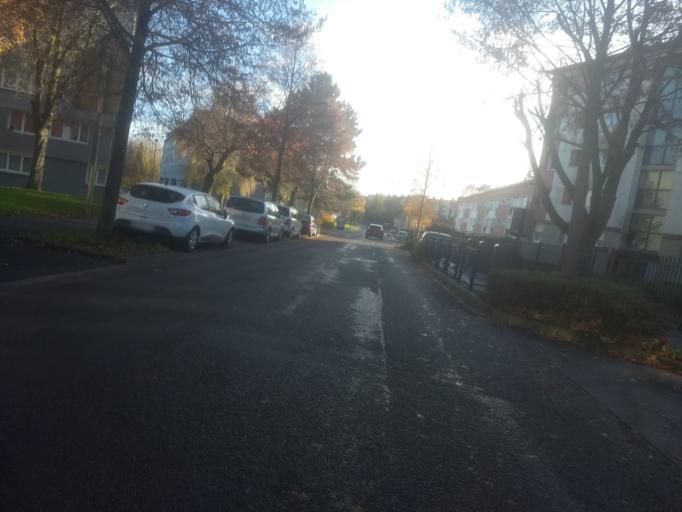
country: FR
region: Nord-Pas-de-Calais
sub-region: Departement du Pas-de-Calais
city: Anzin-Saint-Aubin
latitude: 50.3005
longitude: 2.7478
